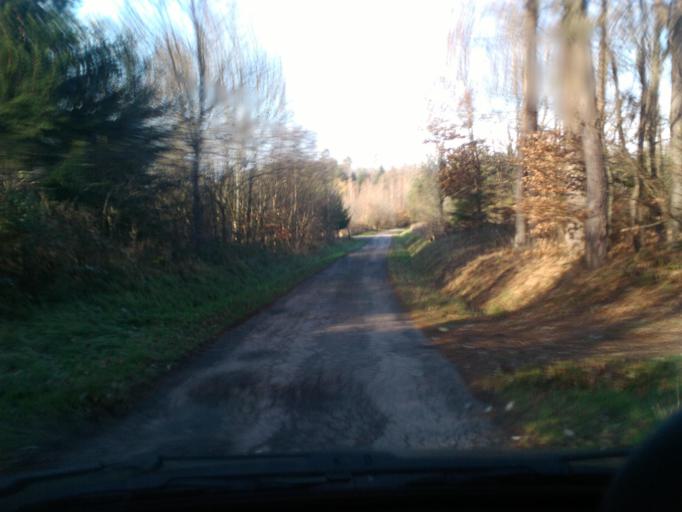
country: FR
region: Lorraine
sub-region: Departement des Vosges
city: Saint-Die-des-Vosges
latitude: 48.3289
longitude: 6.9695
